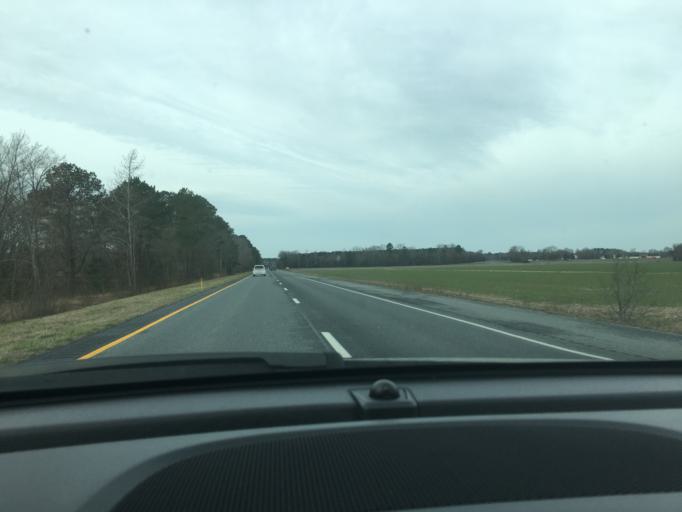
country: US
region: Maryland
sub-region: Wicomico County
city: Pittsville
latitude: 38.3850
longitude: -75.4079
